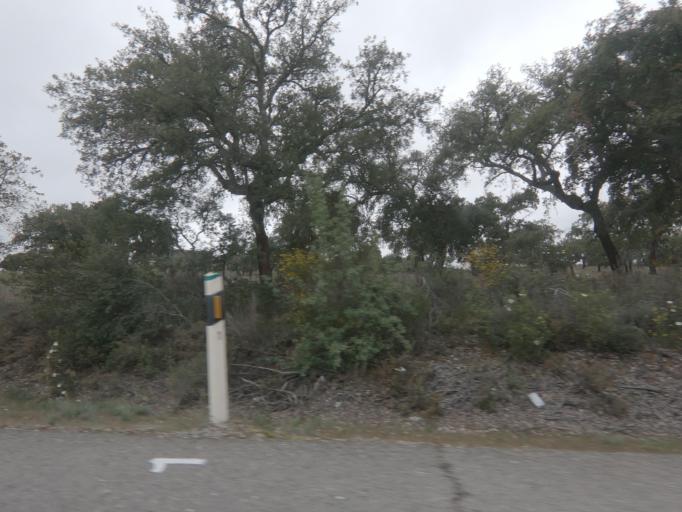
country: ES
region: Extremadura
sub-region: Provincia de Badajoz
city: Puebla de Obando
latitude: 39.2400
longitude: -6.5637
